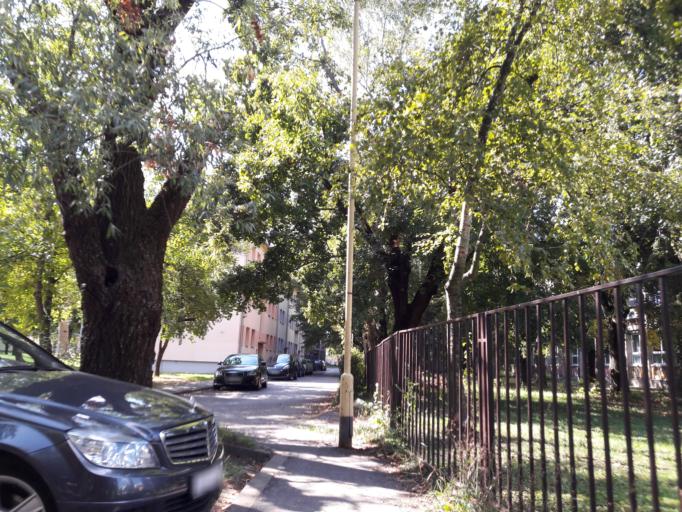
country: HR
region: Osjecko-Baranjska
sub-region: Grad Osijek
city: Osijek
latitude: 45.5563
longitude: 18.7011
